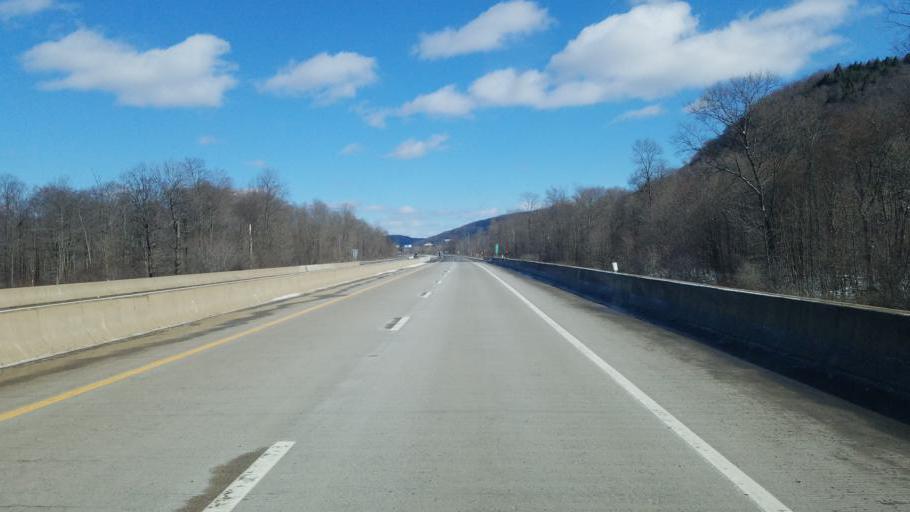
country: US
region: Pennsylvania
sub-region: McKean County
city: Foster Brook
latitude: 42.0863
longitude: -78.6196
